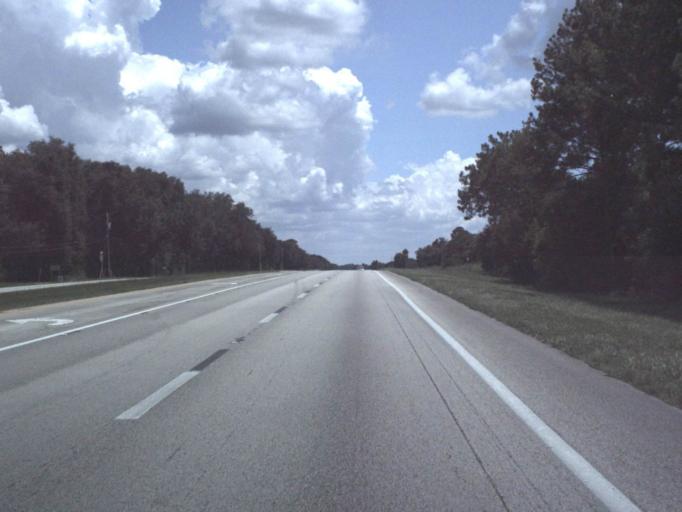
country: US
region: Florida
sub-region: Alachua County
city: Hawthorne
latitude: 29.6315
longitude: -82.1023
